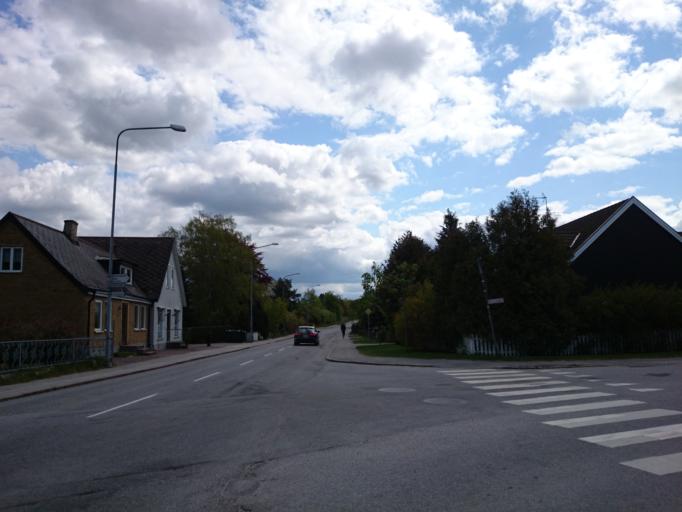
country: SE
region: Skane
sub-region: Lunds Kommun
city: Genarp
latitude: 55.5983
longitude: 13.4048
